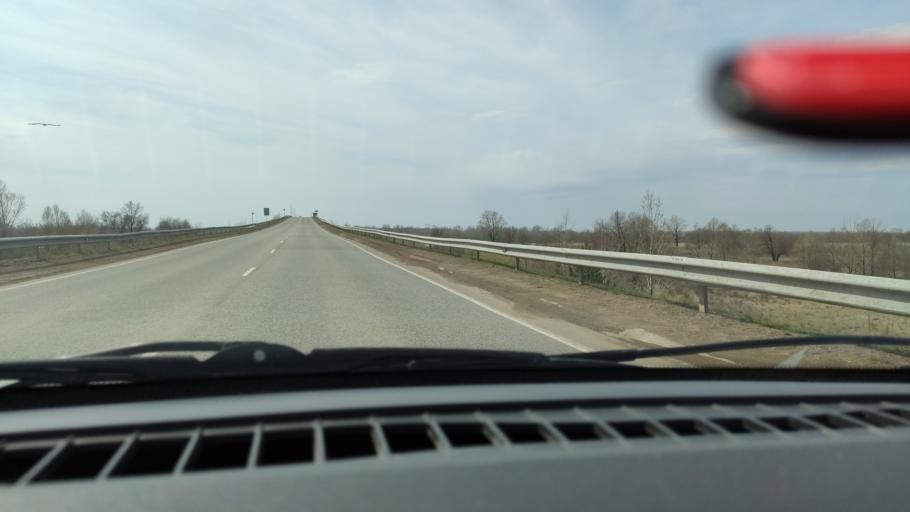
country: RU
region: Bashkortostan
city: Dyurtyuli
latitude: 55.5317
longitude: 54.8511
